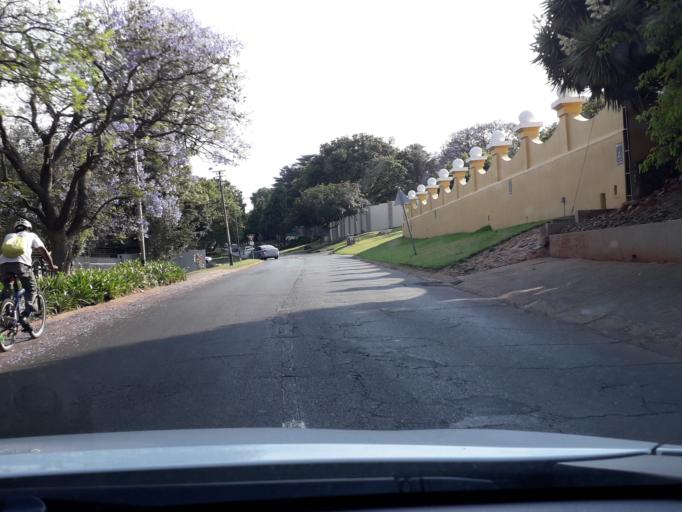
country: ZA
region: Gauteng
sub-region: City of Johannesburg Metropolitan Municipality
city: Roodepoort
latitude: -26.1464
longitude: 27.9582
